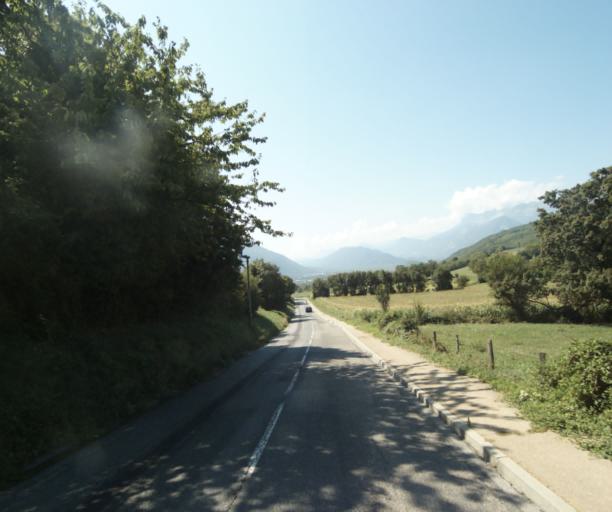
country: FR
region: Rhone-Alpes
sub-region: Departement de l'Isere
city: Jarrie
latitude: 45.1124
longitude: 5.7547
